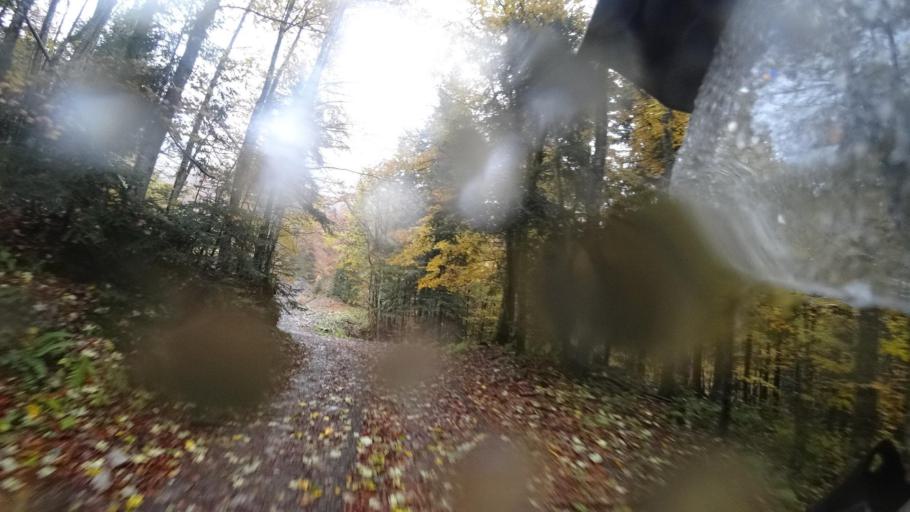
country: HR
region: Primorsko-Goranska
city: Vrbovsko
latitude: 45.2966
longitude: 15.0525
